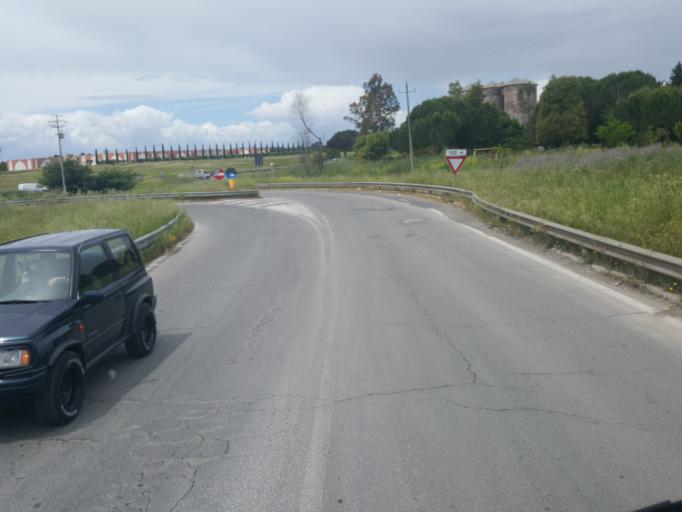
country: IT
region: Latium
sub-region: Provincia di Latina
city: Aprilia
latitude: 41.5701
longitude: 12.6697
